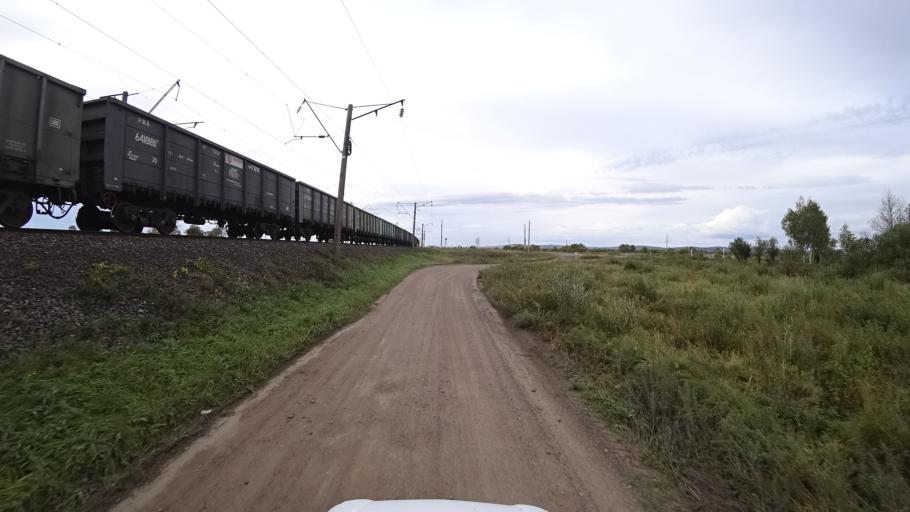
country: RU
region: Amur
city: Arkhara
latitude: 49.3699
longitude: 130.1408
